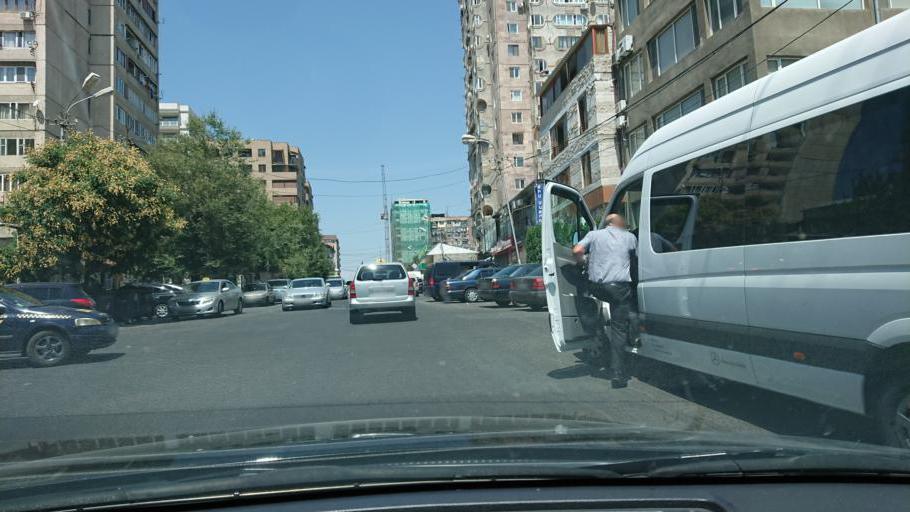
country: AM
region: Yerevan
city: Yerevan
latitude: 40.1978
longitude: 44.5022
